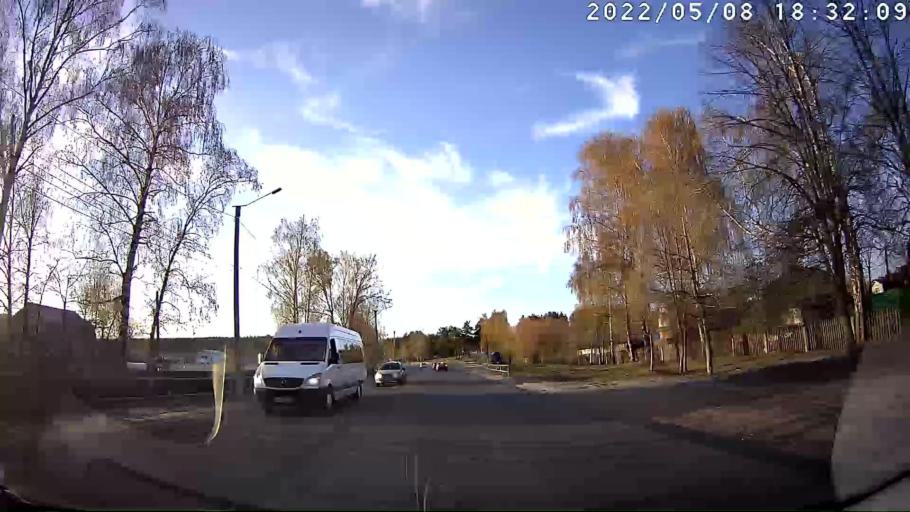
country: RU
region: Mariy-El
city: Volzhsk
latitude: 55.8856
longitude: 48.3597
